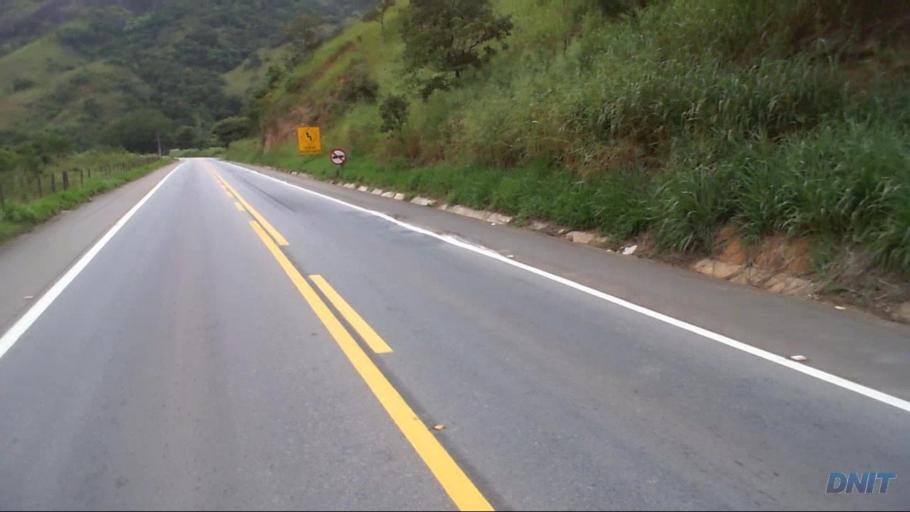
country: BR
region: Minas Gerais
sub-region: Timoteo
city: Timoteo
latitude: -19.5739
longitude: -42.7166
